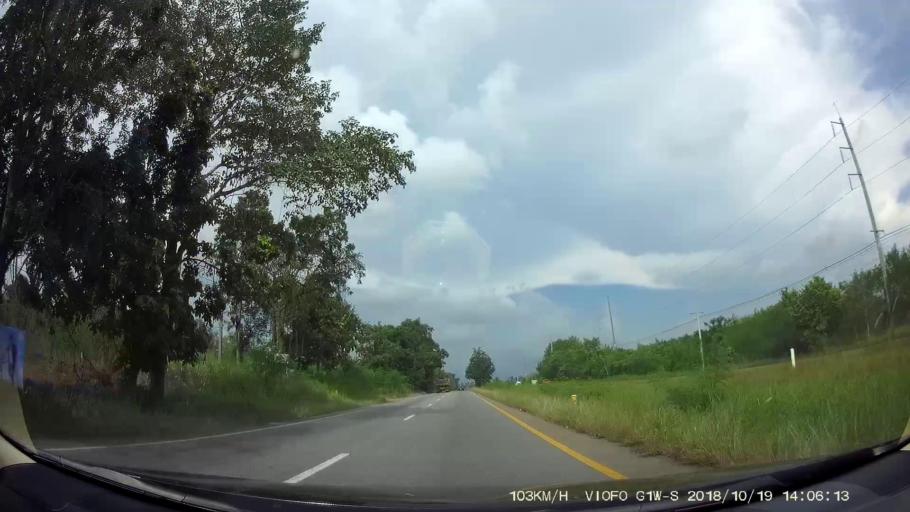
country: TH
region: Chaiyaphum
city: Chaiyaphum
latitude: 15.8844
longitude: 102.1021
